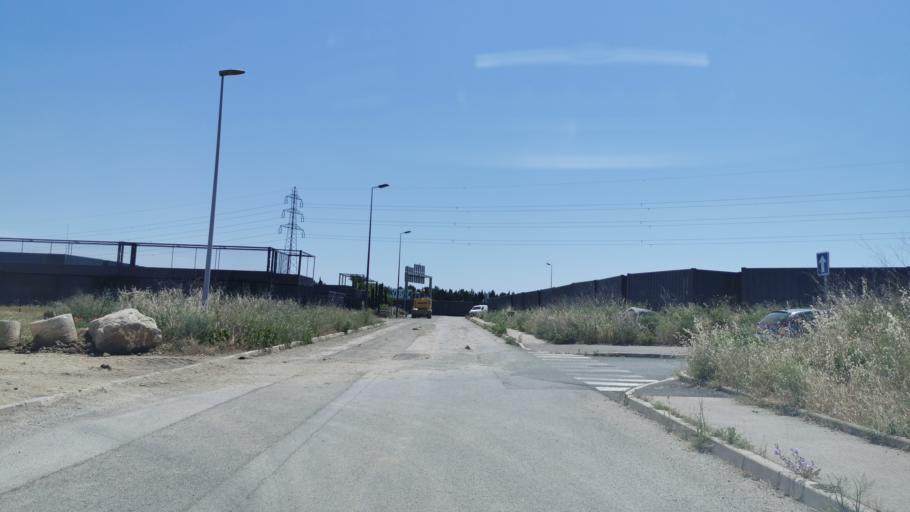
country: FR
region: Languedoc-Roussillon
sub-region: Departement de l'Aude
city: Narbonne
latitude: 43.1659
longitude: 2.9946
